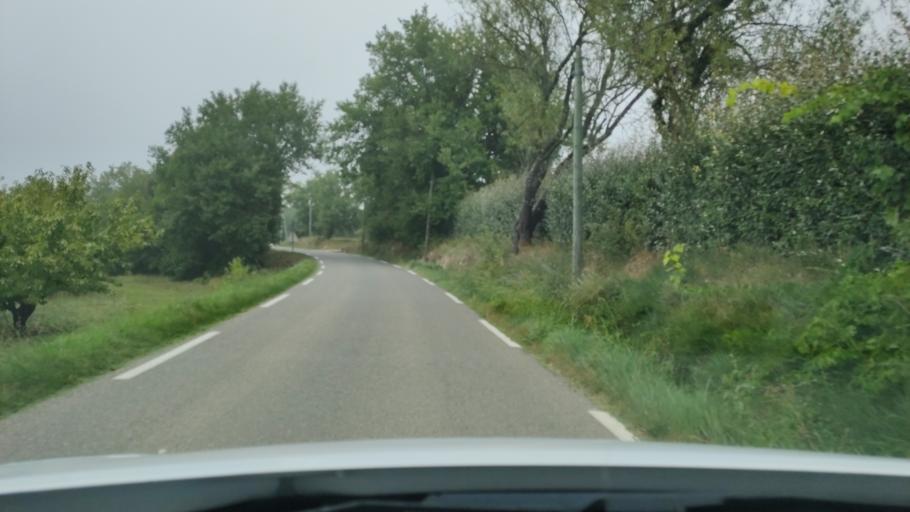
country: FR
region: Provence-Alpes-Cote d'Azur
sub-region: Departement du Vaucluse
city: Bonnieux
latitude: 43.8458
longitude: 5.3104
